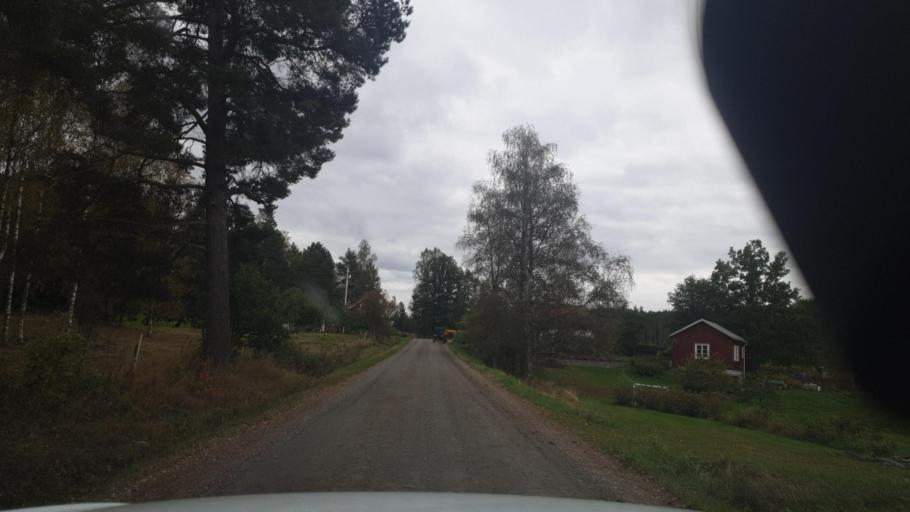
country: SE
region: Vaermland
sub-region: Karlstads Kommun
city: Edsvalla
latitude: 59.5116
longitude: 13.0179
